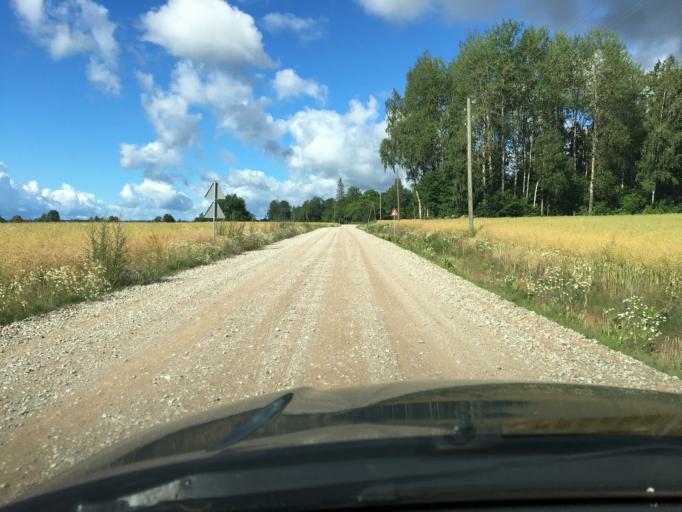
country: LV
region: Kuldigas Rajons
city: Kuldiga
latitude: 56.8426
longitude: 21.9324
